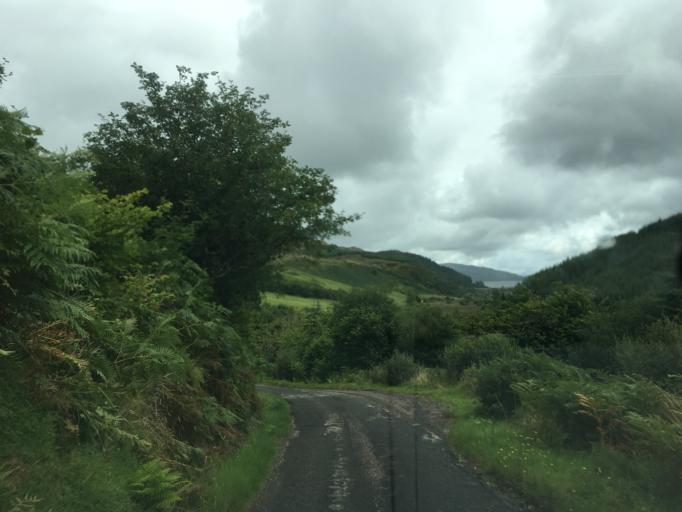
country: GB
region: Scotland
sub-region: Argyll and Bute
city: Oban
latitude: 56.2549
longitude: -5.4065
